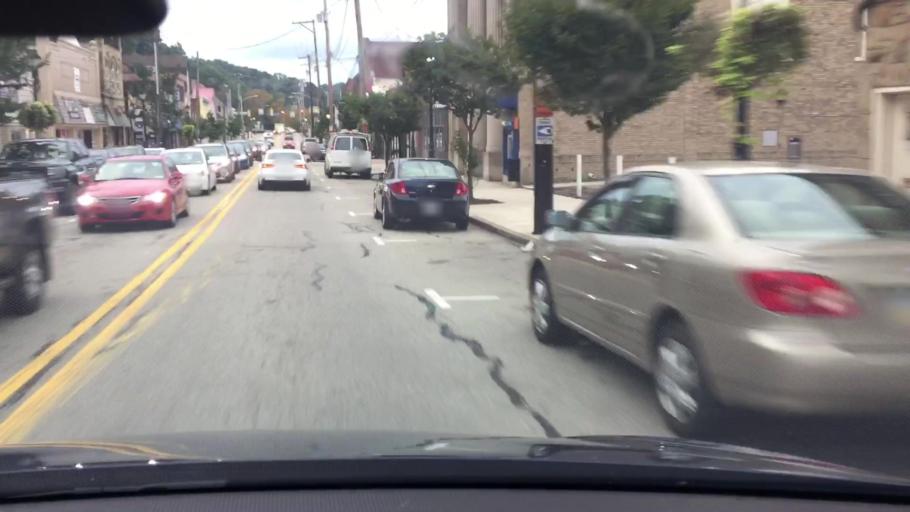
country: US
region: Pennsylvania
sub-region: Allegheny County
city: Verona
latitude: 40.5073
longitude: -79.8429
